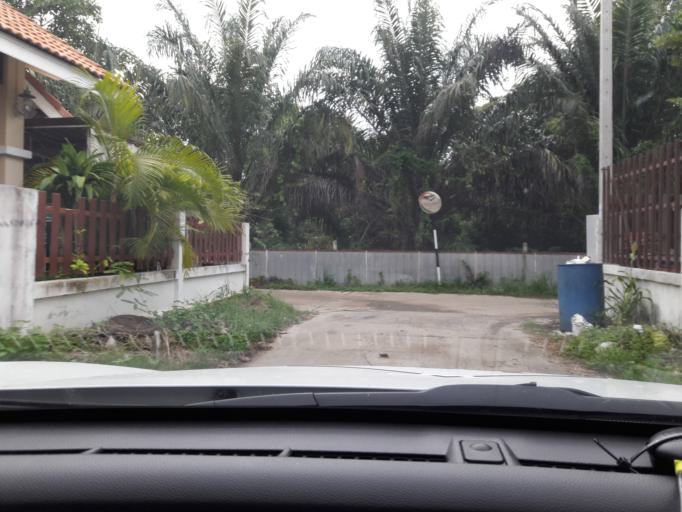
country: TH
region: Nakhon Sawan
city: Tak Fa
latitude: 15.3440
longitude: 100.5024
